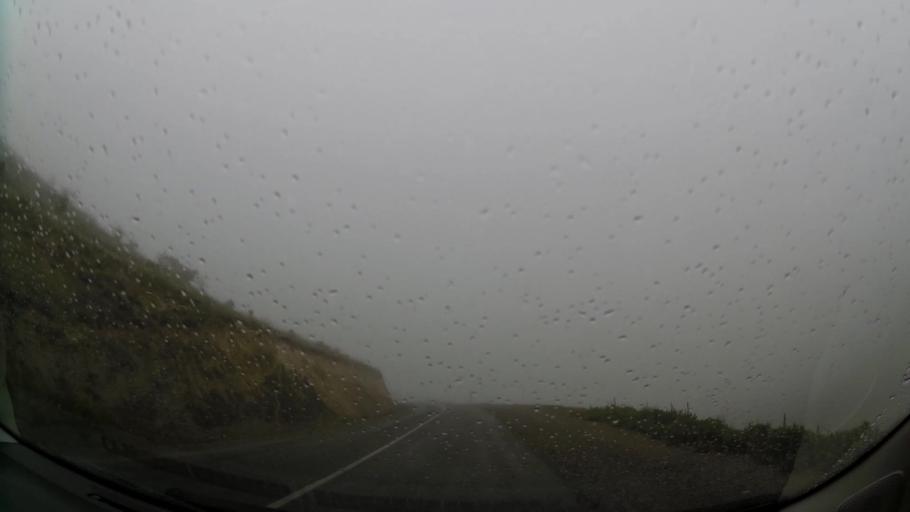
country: MA
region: Oriental
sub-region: Nador
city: Boudinar
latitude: 35.0952
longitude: -3.5325
